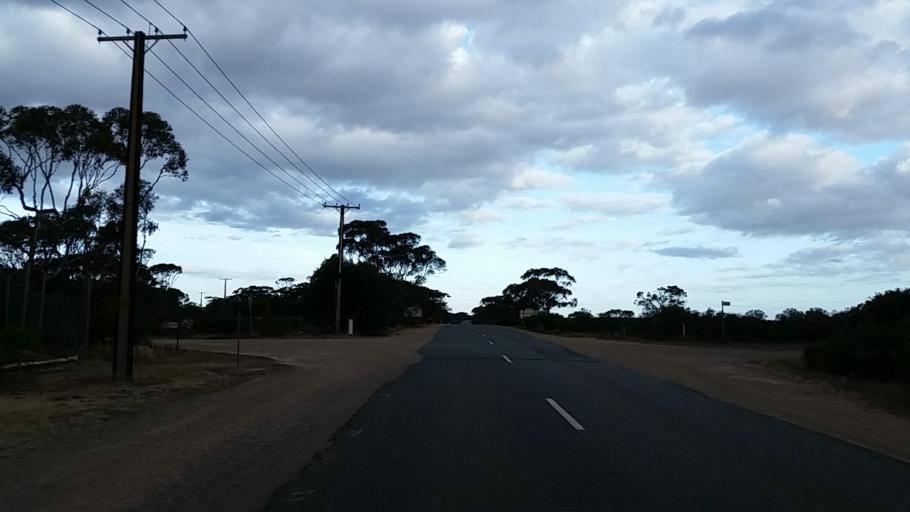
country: AU
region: South Australia
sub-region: Barossa
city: Angaston
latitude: -34.5728
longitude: 139.3037
